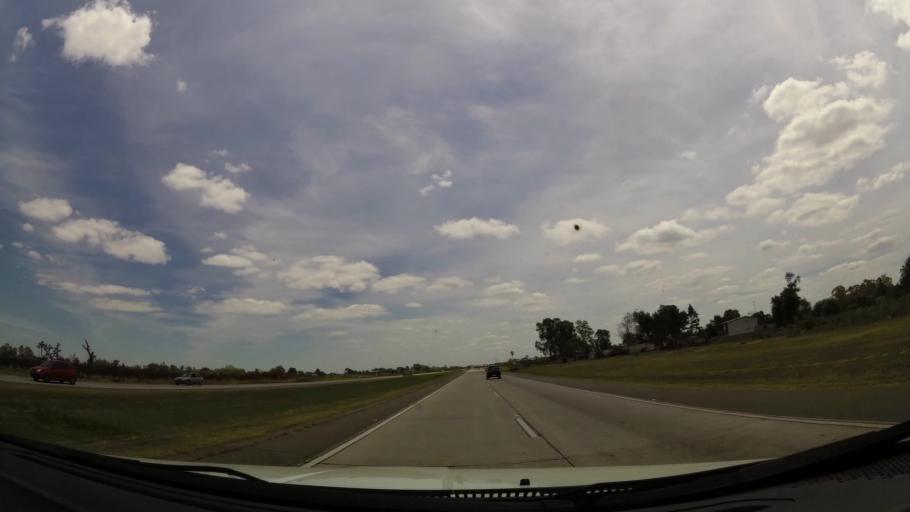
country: UY
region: San Jose
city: Delta del Tigre
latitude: -34.7655
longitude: -56.4015
